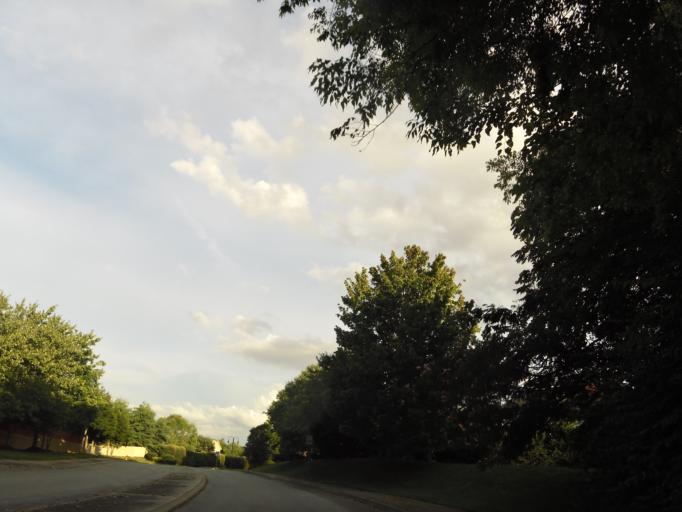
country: US
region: Tennessee
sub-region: Knox County
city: Farragut
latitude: 35.8766
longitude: -84.1670
